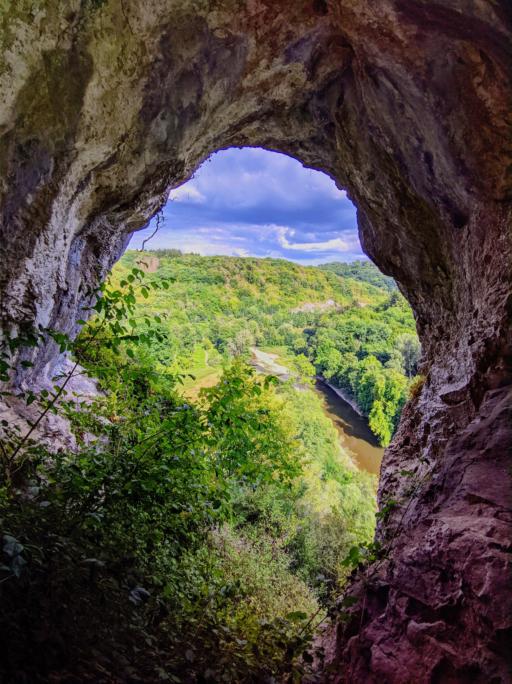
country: BE
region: Wallonia
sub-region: Province de Namur
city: Houyet
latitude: 50.2145
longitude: 4.9570
